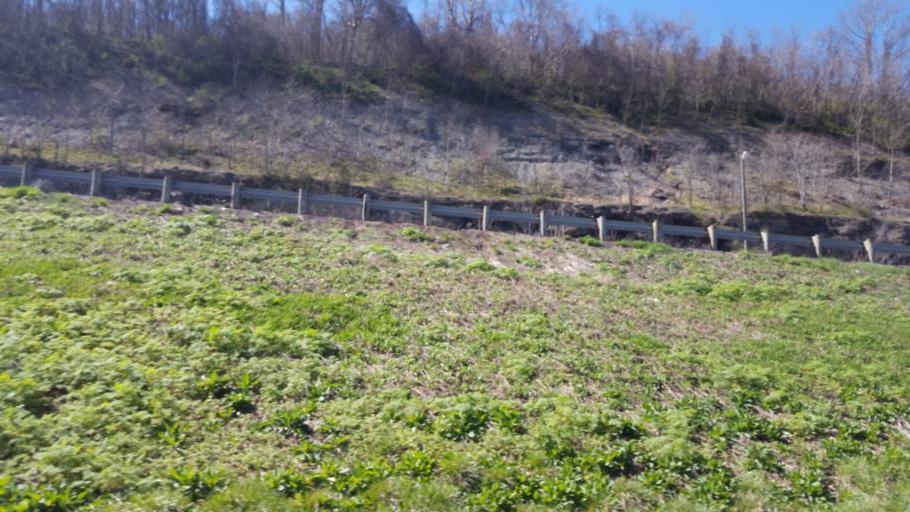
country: US
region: Ohio
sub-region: Jefferson County
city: Tiltonsville
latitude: 40.1751
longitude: -80.6982
